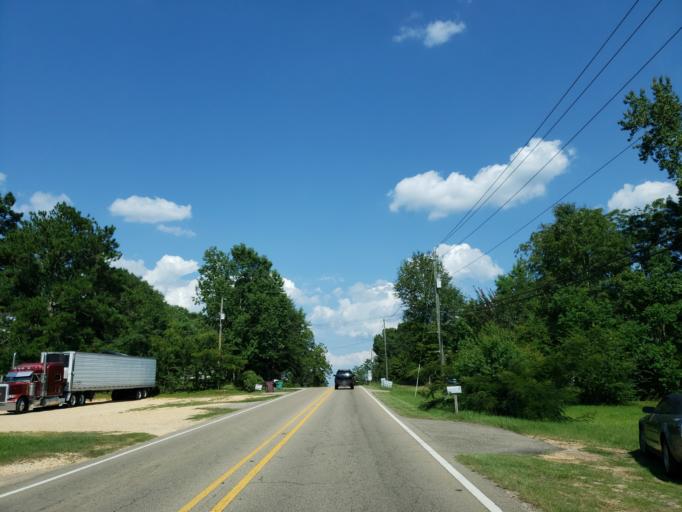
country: US
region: Mississippi
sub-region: Covington County
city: Collins
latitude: 31.5618
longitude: -89.4954
